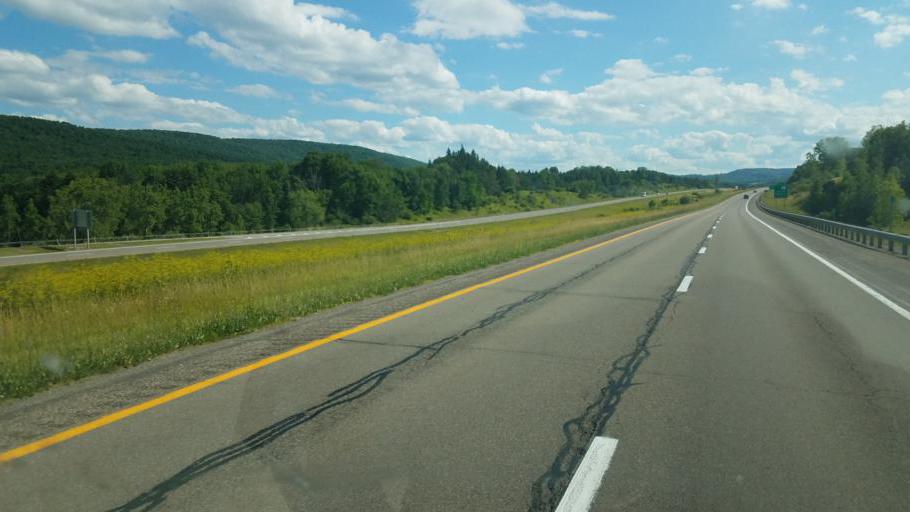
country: US
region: New York
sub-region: Steuben County
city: Hornell
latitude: 42.3406
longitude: -77.7284
